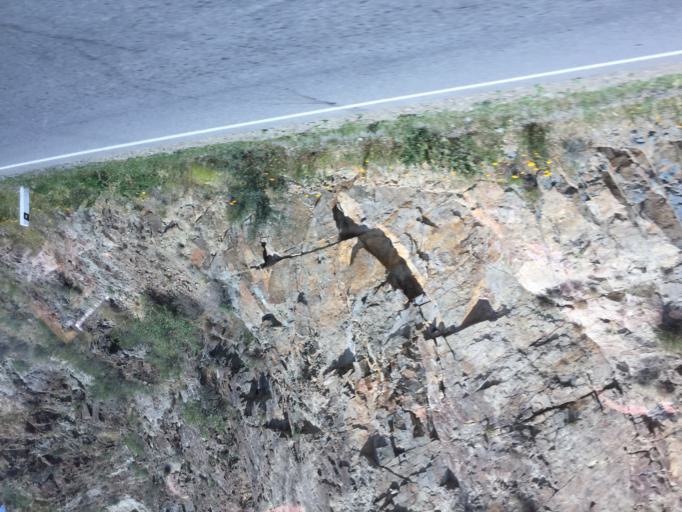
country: AM
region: Vayots' Dzori Marz
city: Jermuk
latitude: 39.7202
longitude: 45.6369
